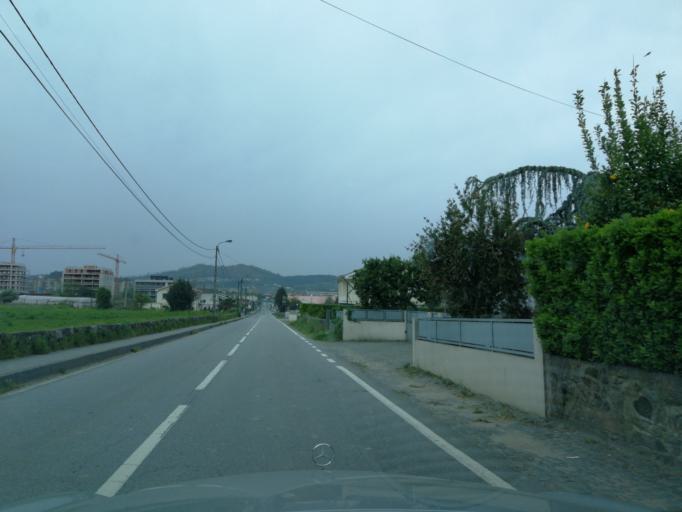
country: PT
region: Braga
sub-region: Braga
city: Braga
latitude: 41.5649
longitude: -8.4405
